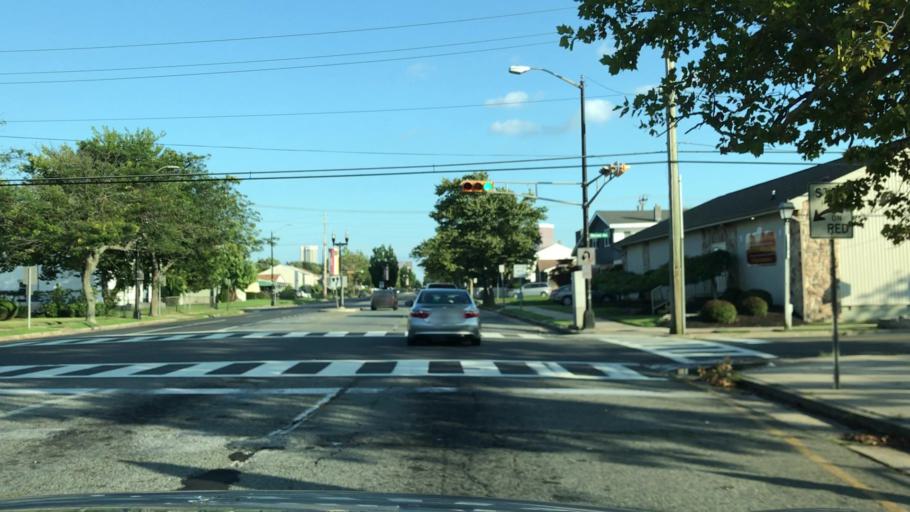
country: US
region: New Jersey
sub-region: Atlantic County
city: Atlantic City
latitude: 39.3707
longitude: -74.4387
